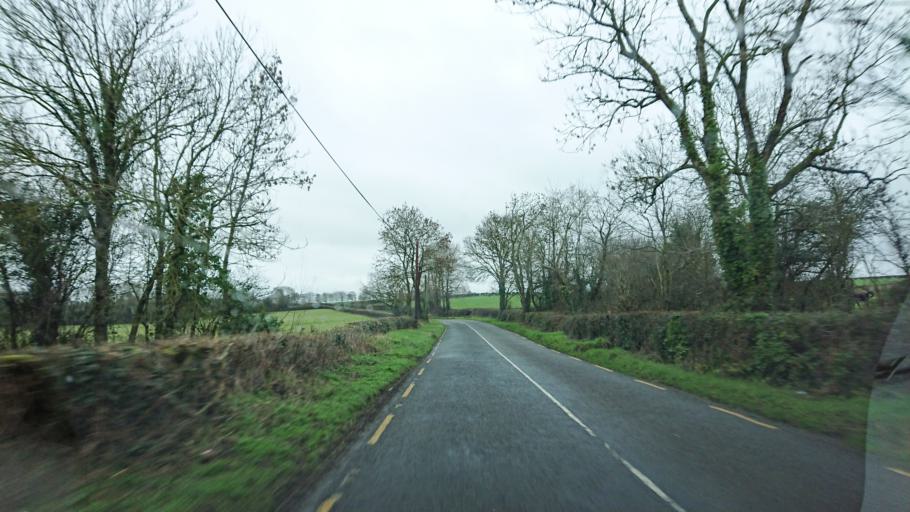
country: IE
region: Leinster
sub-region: Kilkenny
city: Callan
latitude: 52.5317
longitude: -7.2957
